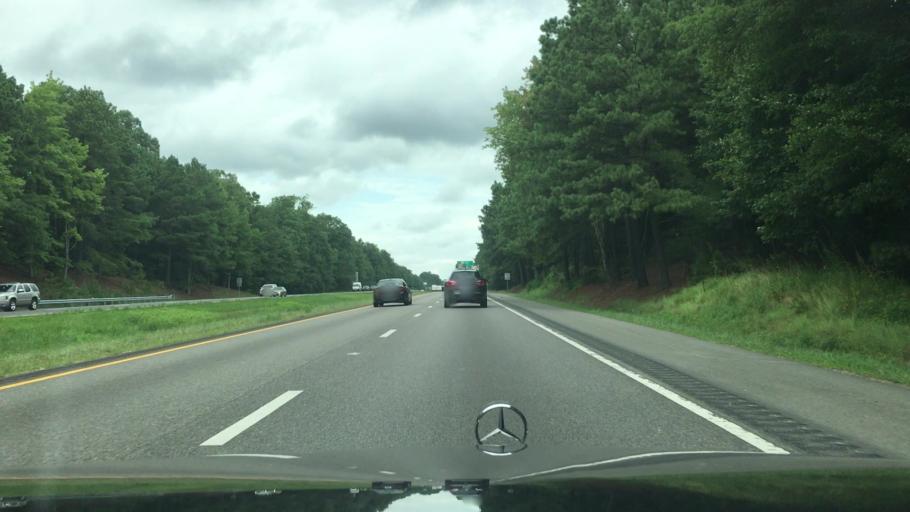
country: US
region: Virginia
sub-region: Chesterfield County
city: Brandermill
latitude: 37.4332
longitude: -77.6336
